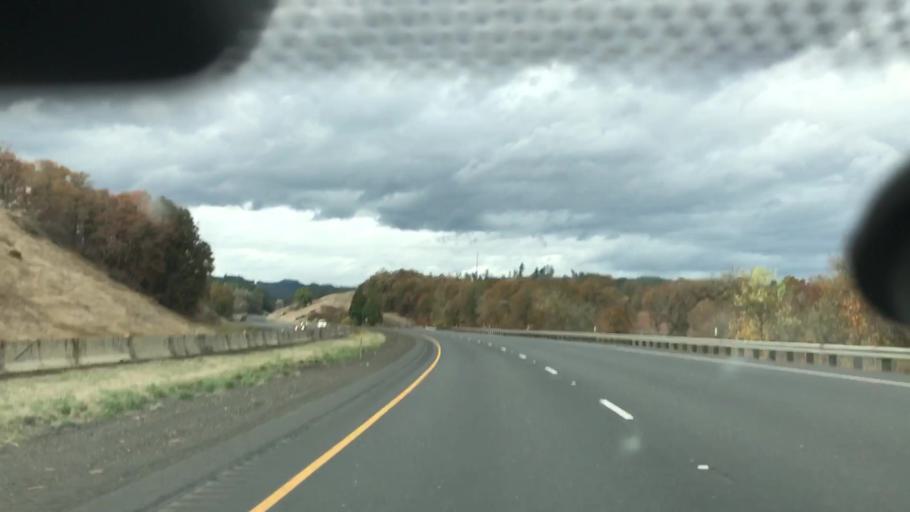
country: US
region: Oregon
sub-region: Douglas County
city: Sutherlin
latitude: 43.4727
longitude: -123.3163
